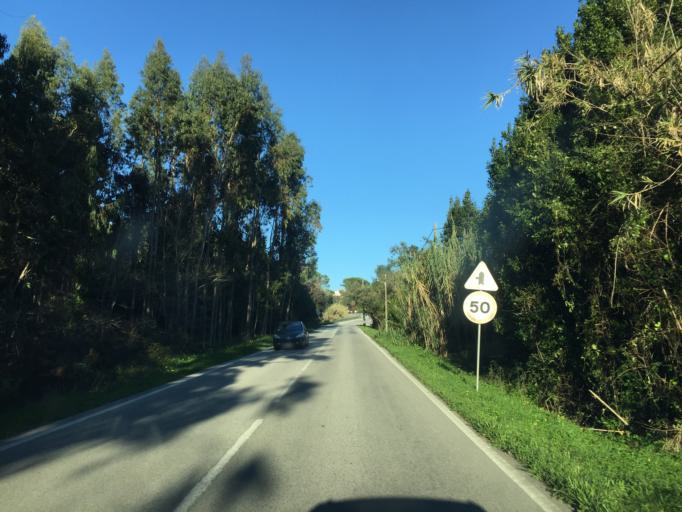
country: PT
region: Coimbra
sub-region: Figueira da Foz
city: Alhadas
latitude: 40.1732
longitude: -8.8031
